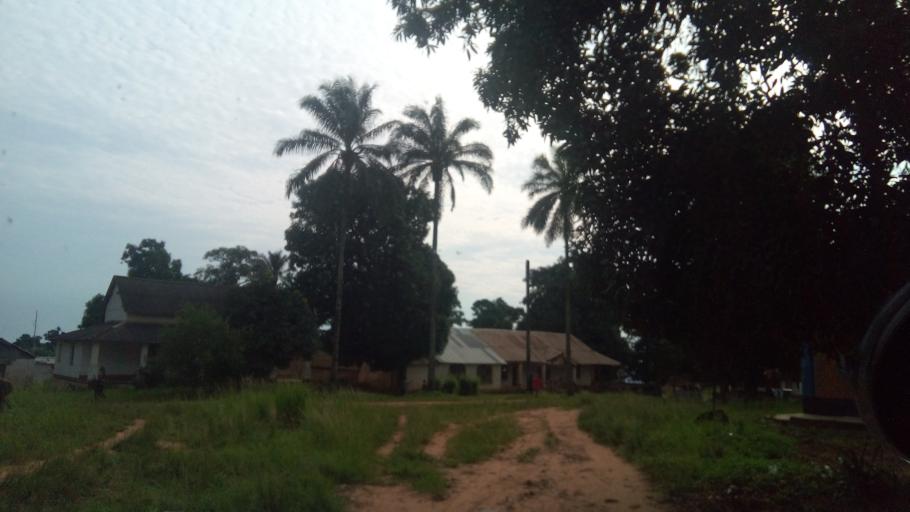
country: CD
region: Kasai-Oriental
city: Kabinda
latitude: -6.1338
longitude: 24.4860
